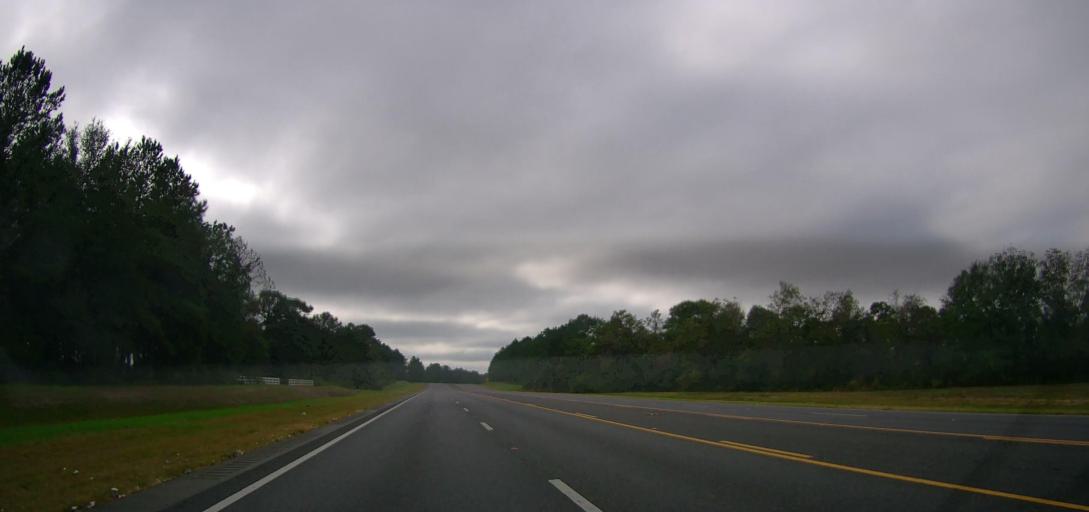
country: US
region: Georgia
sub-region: Colquitt County
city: Moultrie
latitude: 31.0491
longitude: -83.8392
